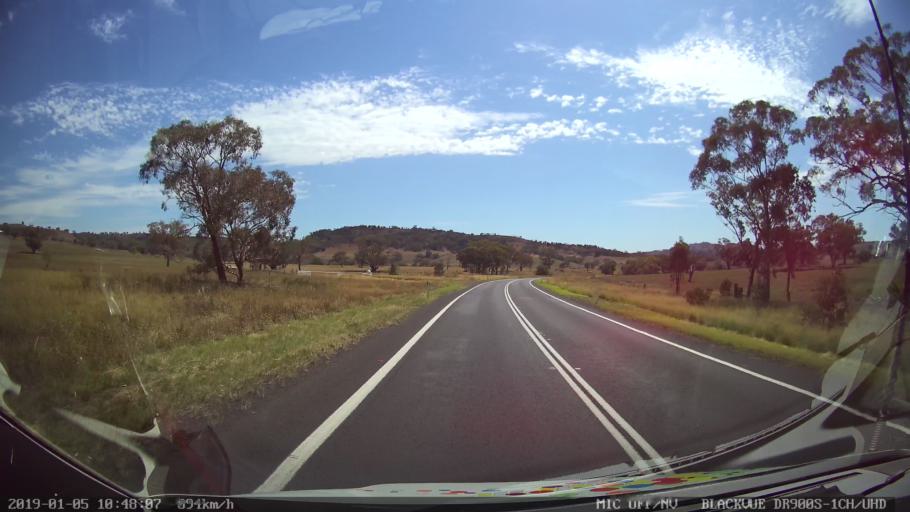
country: AU
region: New South Wales
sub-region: Warrumbungle Shire
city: Coonabarabran
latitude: -31.4389
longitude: 149.0414
